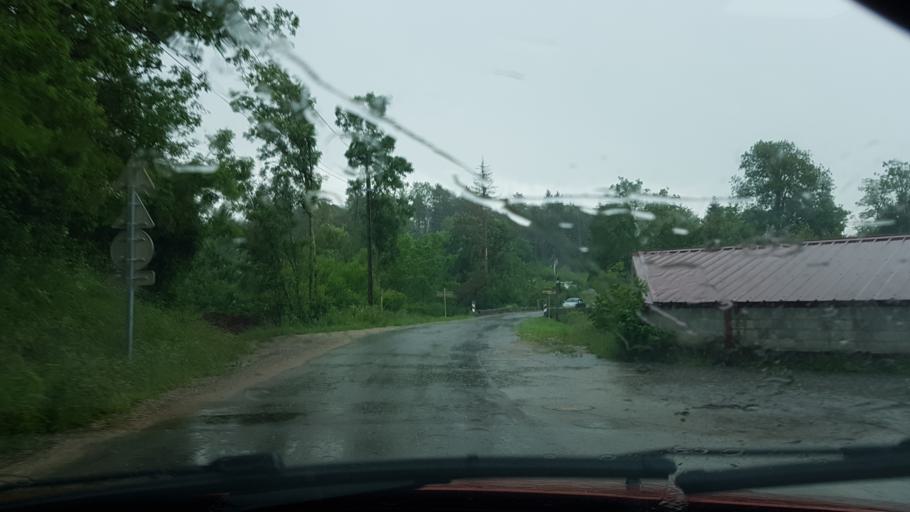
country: FR
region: Franche-Comte
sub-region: Departement du Jura
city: Clairvaux-les-Lacs
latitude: 46.5814
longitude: 5.7039
